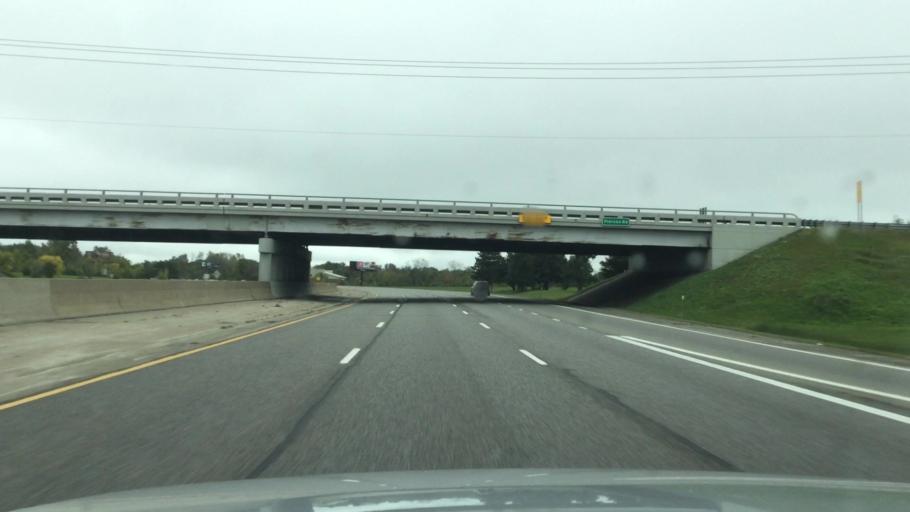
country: US
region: Michigan
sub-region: Genesee County
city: Beecher
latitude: 43.0613
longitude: -83.7626
